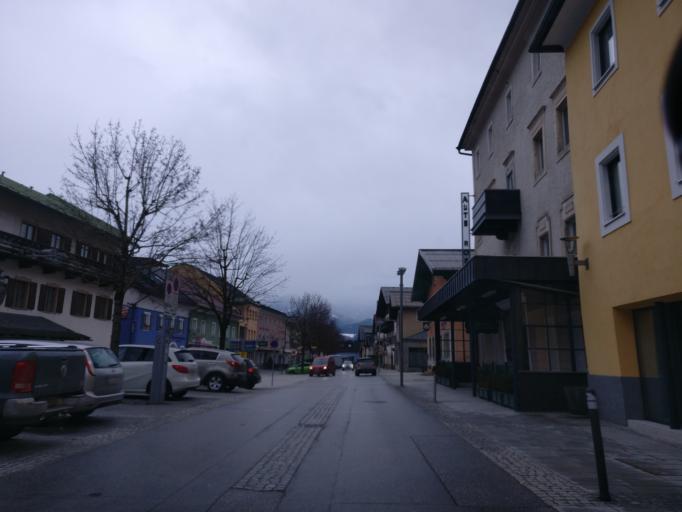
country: AT
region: Salzburg
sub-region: Politischer Bezirk Sankt Johann im Pongau
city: Werfen
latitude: 47.4767
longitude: 13.1891
